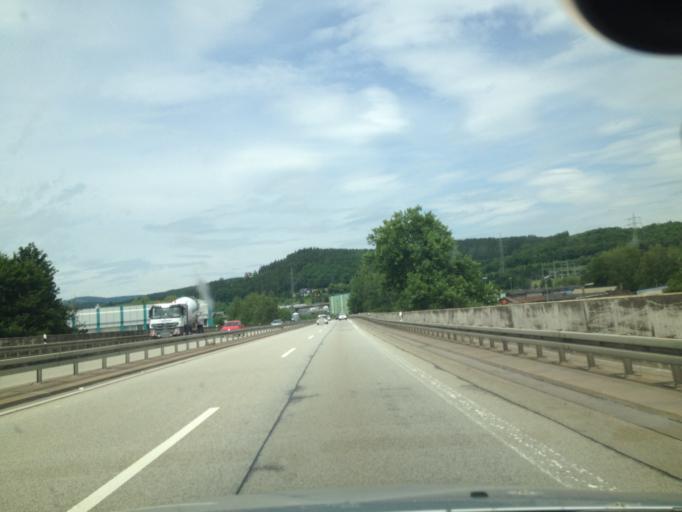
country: DE
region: North Rhine-Westphalia
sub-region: Regierungsbezirk Arnsberg
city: Siegen
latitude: 50.9187
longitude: 8.0139
